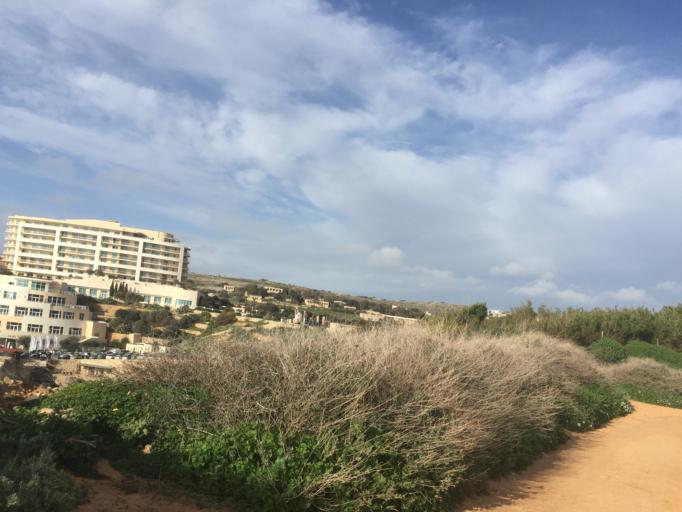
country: MT
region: L-Imgarr
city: Imgarr
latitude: 35.9327
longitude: 14.3443
